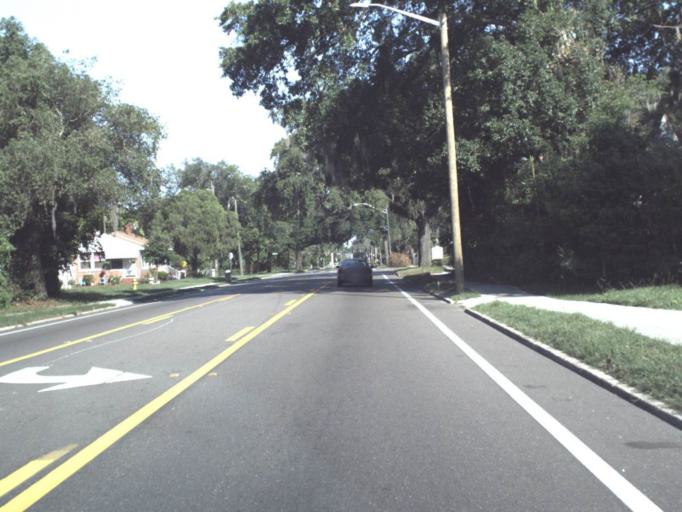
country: US
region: Florida
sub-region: Duval County
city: Jacksonville
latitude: 30.3885
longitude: -81.6604
